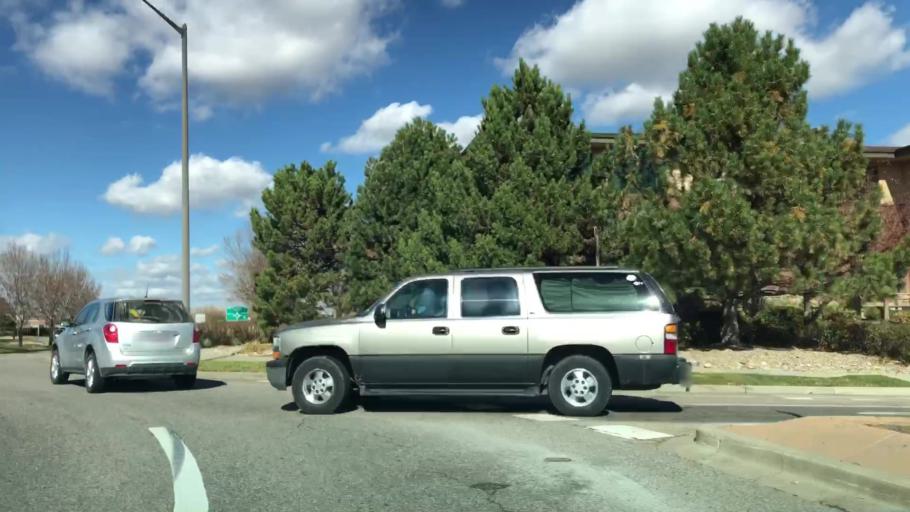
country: US
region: Colorado
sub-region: Larimer County
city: Loveland
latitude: 40.4092
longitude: -105.0020
